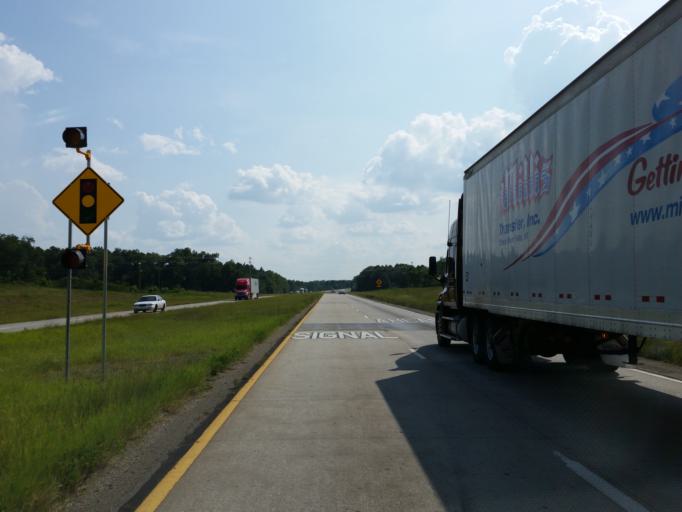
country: US
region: Georgia
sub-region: Crisp County
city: Cordele
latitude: 31.9286
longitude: -83.7571
